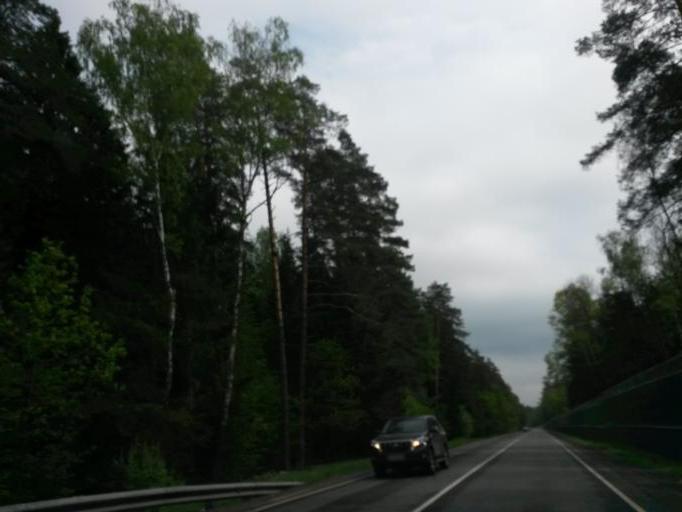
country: RU
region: Moskovskaya
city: Domodedovo
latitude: 55.3665
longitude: 37.7068
